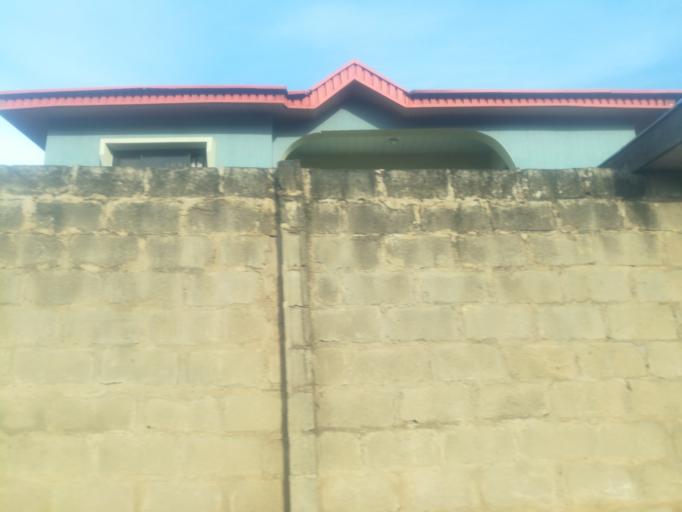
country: NG
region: Oyo
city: Ibadan
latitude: 7.3373
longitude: 3.8901
